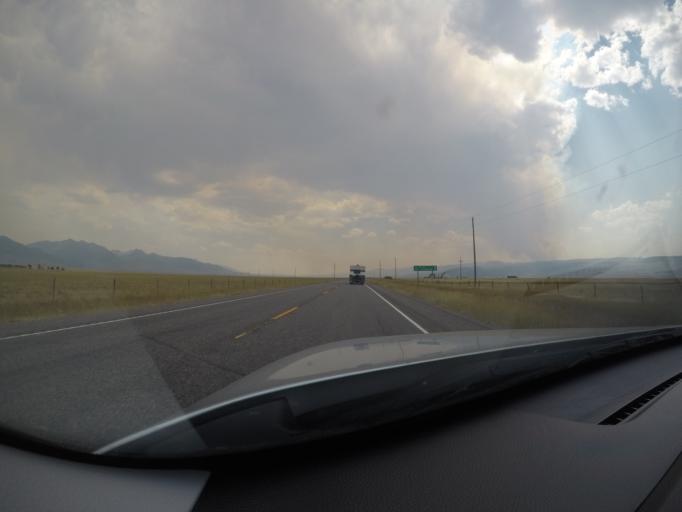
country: US
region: Montana
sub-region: Madison County
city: Virginia City
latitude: 45.1650
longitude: -111.6787
